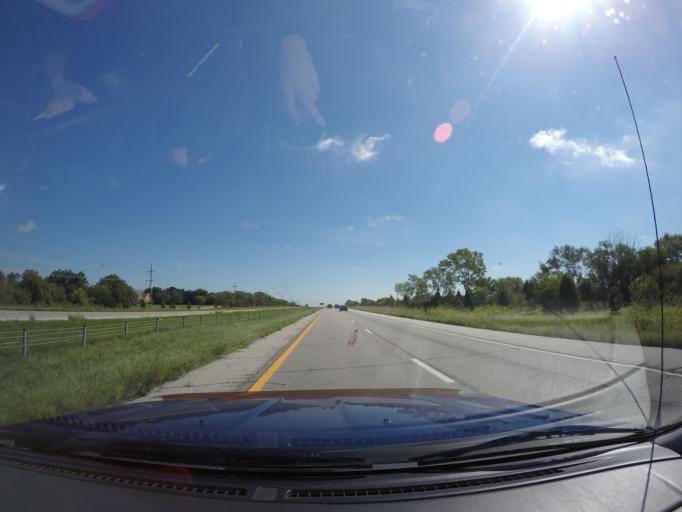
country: US
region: Kansas
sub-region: Johnson County
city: Olathe
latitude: 38.9413
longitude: -94.8403
